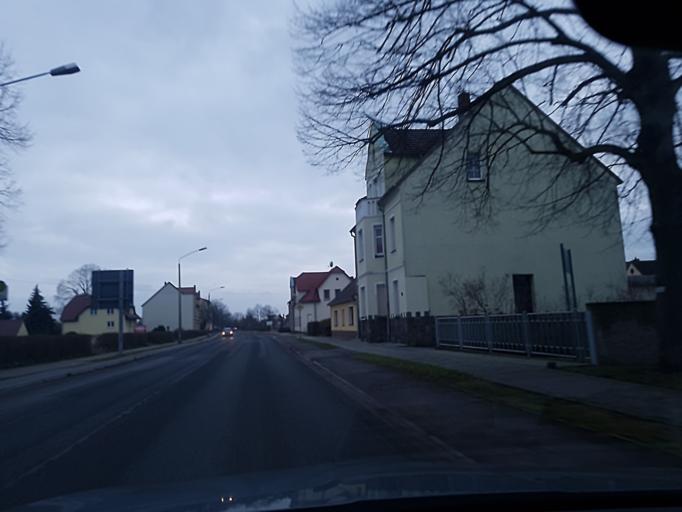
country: DE
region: Brandenburg
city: Doberlug-Kirchhain
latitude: 51.6177
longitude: 13.5597
